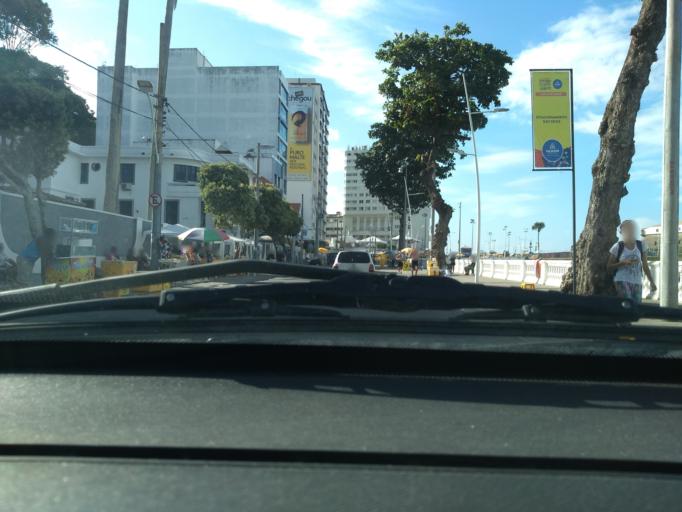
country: BR
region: Bahia
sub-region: Salvador
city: Salvador
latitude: -13.0077
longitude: -38.5326
